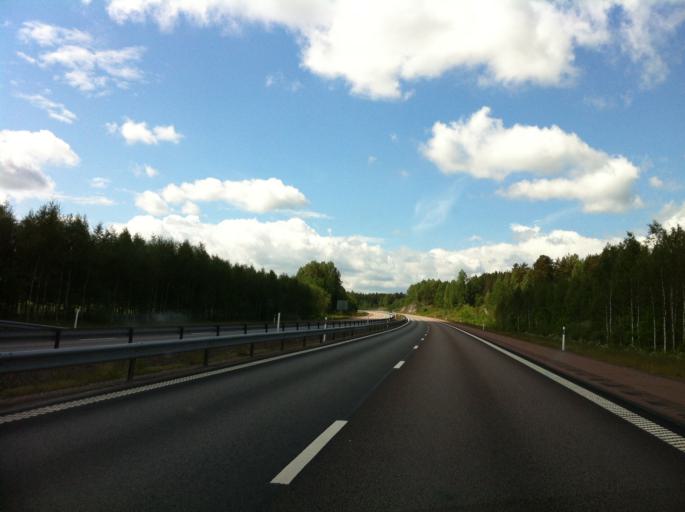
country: SE
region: Vaermland
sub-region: Grums Kommun
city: Slottsbron
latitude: 59.2816
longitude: 13.0281
